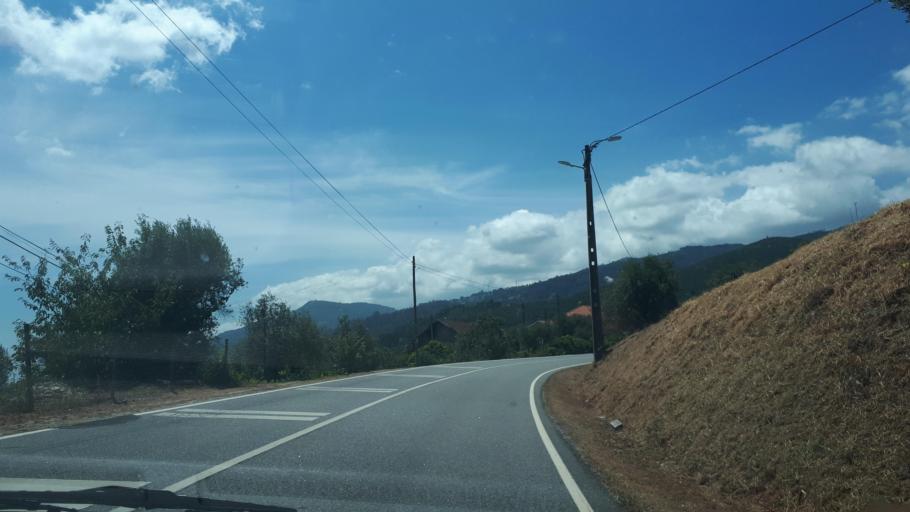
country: PT
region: Viseu
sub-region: Concelho de Tondela
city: Tondela
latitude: 40.5924
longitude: -8.1150
